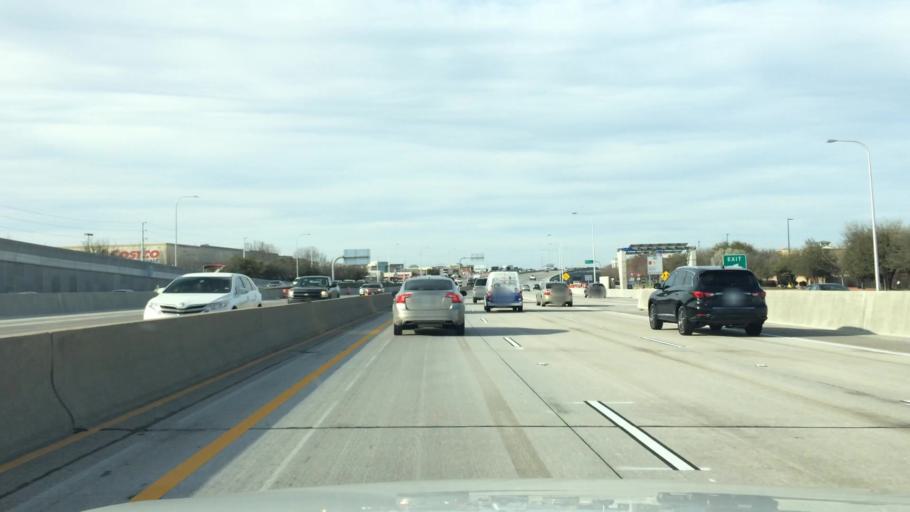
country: US
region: Texas
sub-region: Dallas County
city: Addison
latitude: 33.0220
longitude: -96.8297
